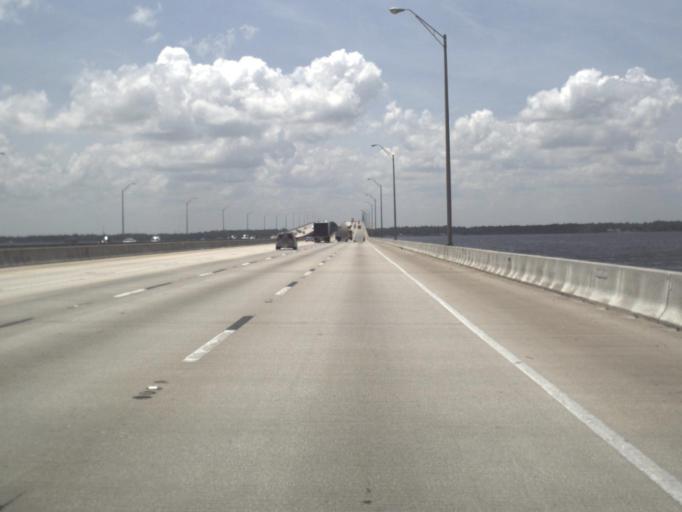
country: US
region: Florida
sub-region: Clay County
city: Orange Park
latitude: 30.1895
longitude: -81.6535
